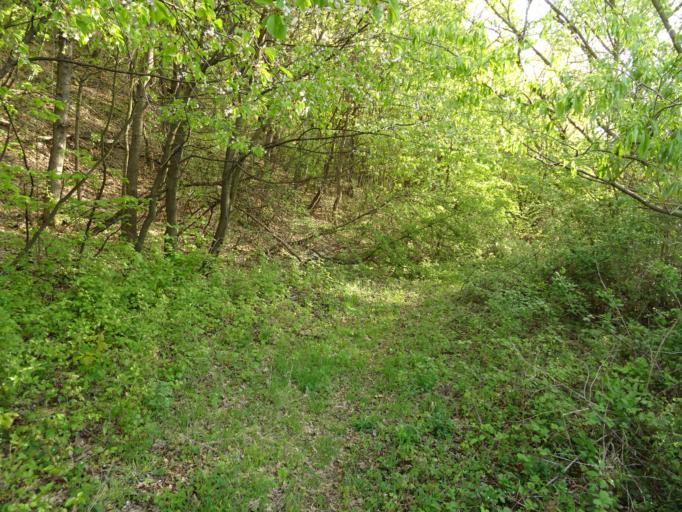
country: HU
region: Borsod-Abauj-Zemplen
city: Gonc
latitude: 48.5507
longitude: 21.4881
